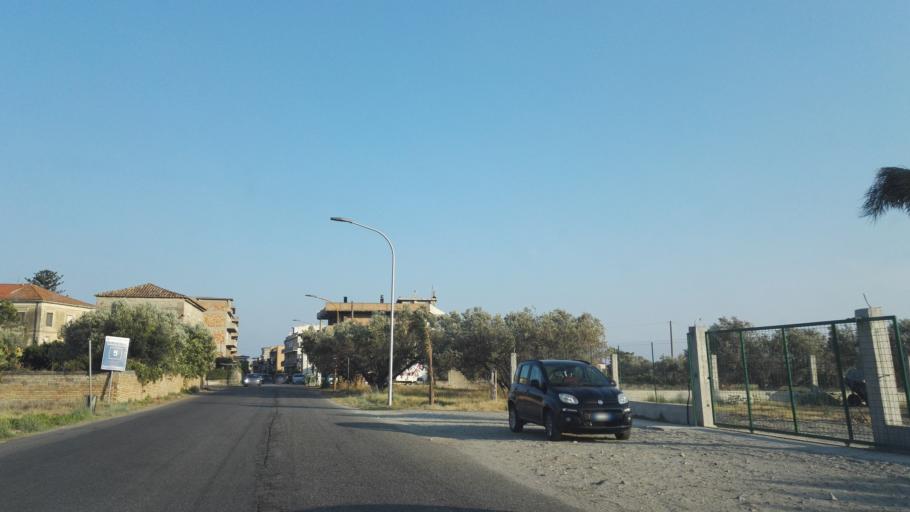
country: IT
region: Calabria
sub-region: Provincia di Reggio Calabria
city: Marina di Gioiosa Ionica
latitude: 38.3041
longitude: 16.3241
